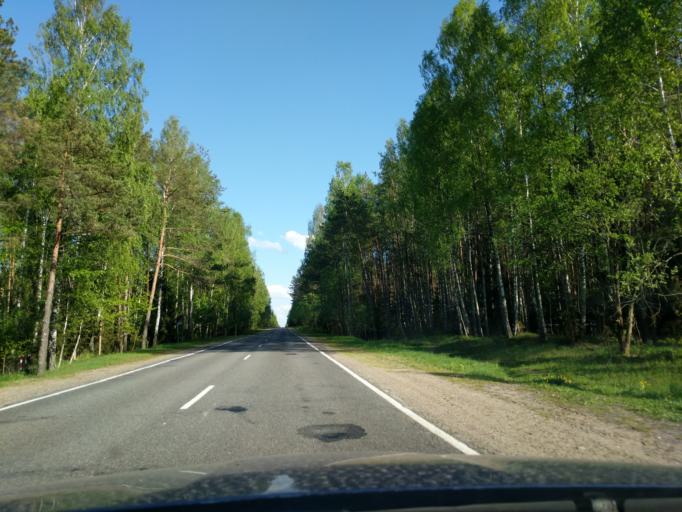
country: BY
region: Minsk
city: Myadzyel
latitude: 54.8126
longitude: 26.9764
